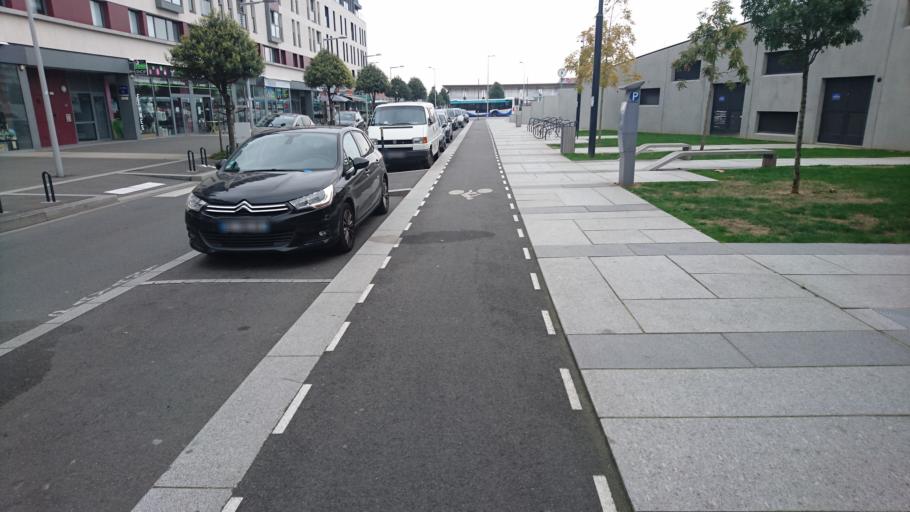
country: FR
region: Brittany
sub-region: Departement d'Ille-et-Vilaine
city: Saint-Malo
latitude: 48.6473
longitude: -2.0061
